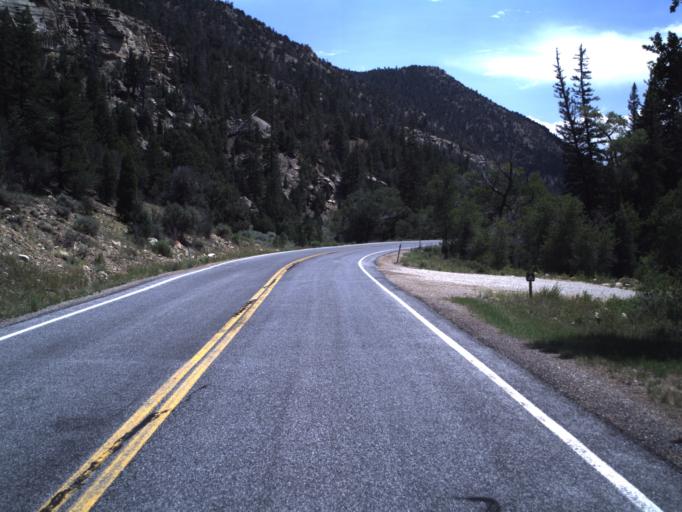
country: US
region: Utah
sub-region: Emery County
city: Huntington
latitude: 39.4466
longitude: -111.1377
